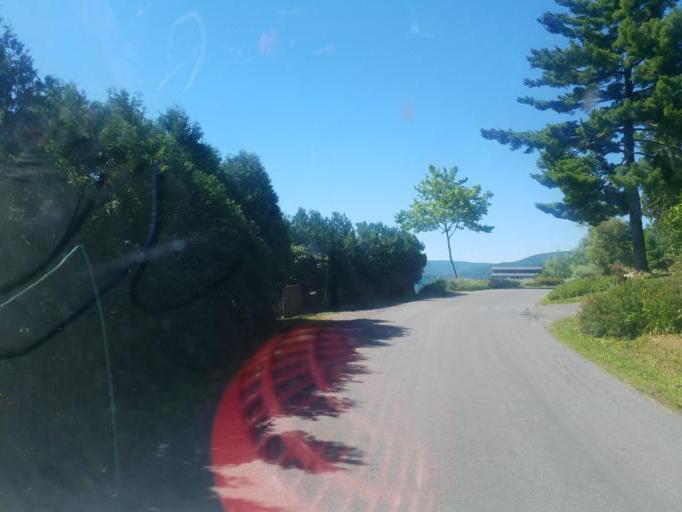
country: US
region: New York
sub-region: Ontario County
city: Naples
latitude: 42.7296
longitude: -77.3513
